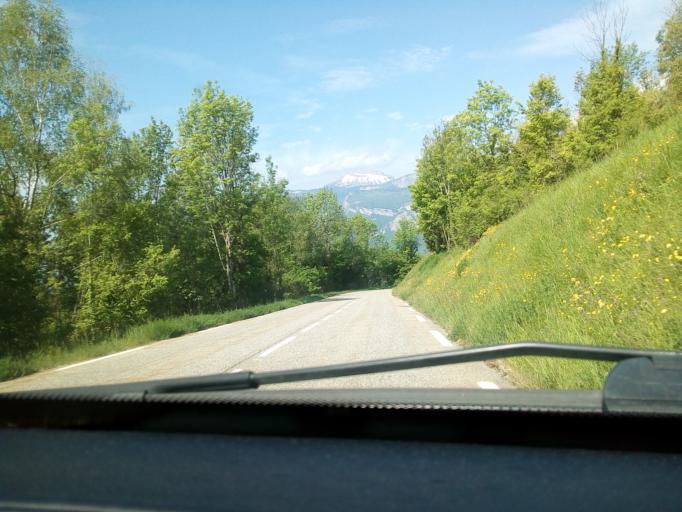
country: FR
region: Rhone-Alpes
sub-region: Departement de l'Isere
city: Le Champ-pres-Froges
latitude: 45.2708
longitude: 5.9428
